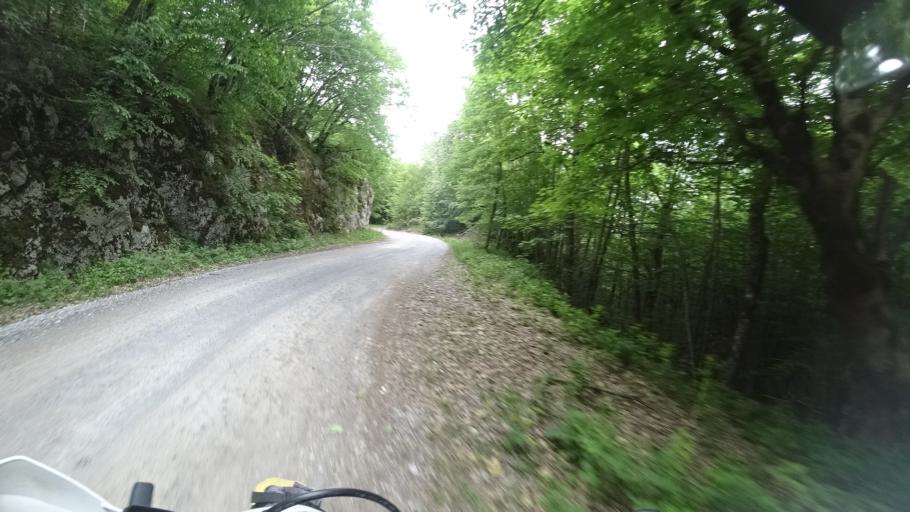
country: HR
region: Zadarska
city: Obrovac
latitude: 44.3034
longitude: 15.6593
